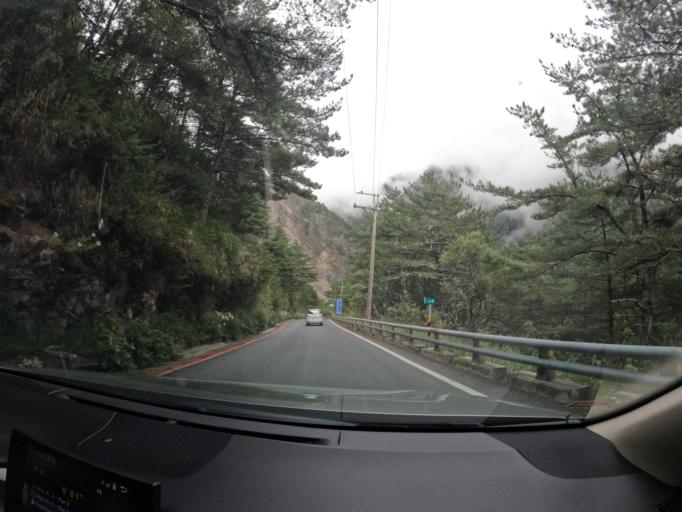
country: TW
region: Taiwan
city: Lugu
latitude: 23.2696
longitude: 120.9728
